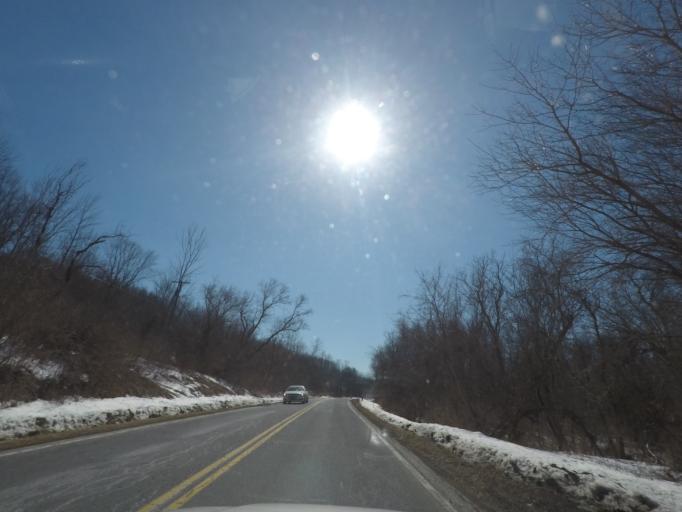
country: US
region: New York
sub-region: Saratoga County
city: Stillwater
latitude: 42.9562
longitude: -73.6232
